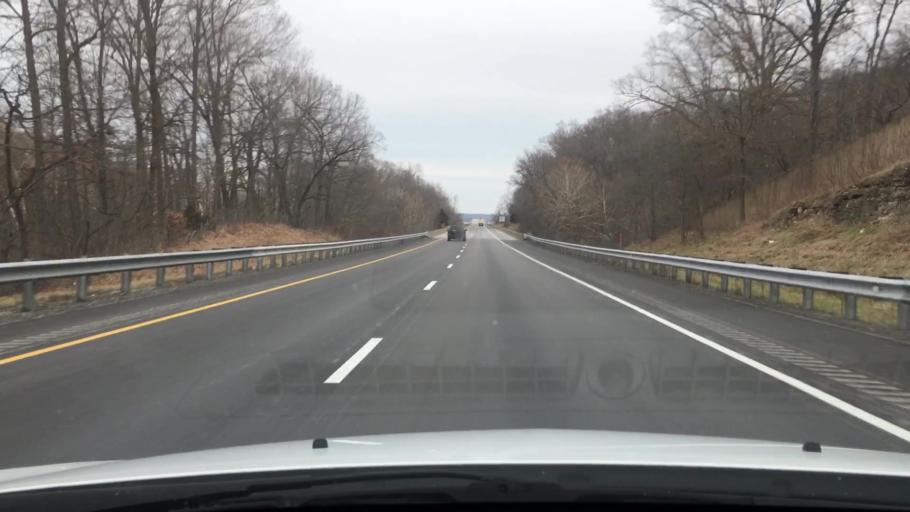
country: US
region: Illinois
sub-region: Pike County
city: Griggsville
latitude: 39.6827
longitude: -90.6517
